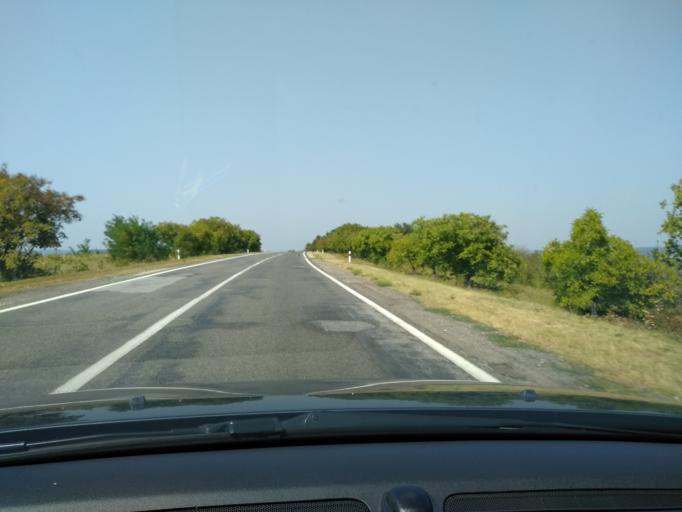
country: MD
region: Chisinau
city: Vatra
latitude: 47.0106
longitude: 28.6431
